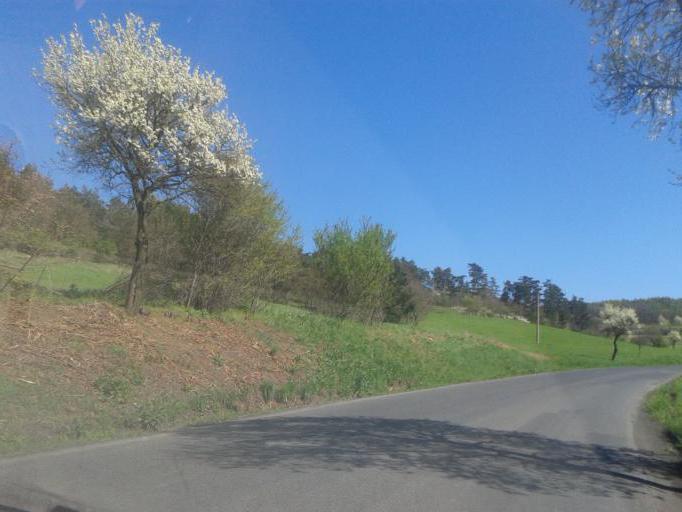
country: CZ
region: Central Bohemia
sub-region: Okres Beroun
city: Beroun
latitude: 49.9283
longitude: 14.0674
